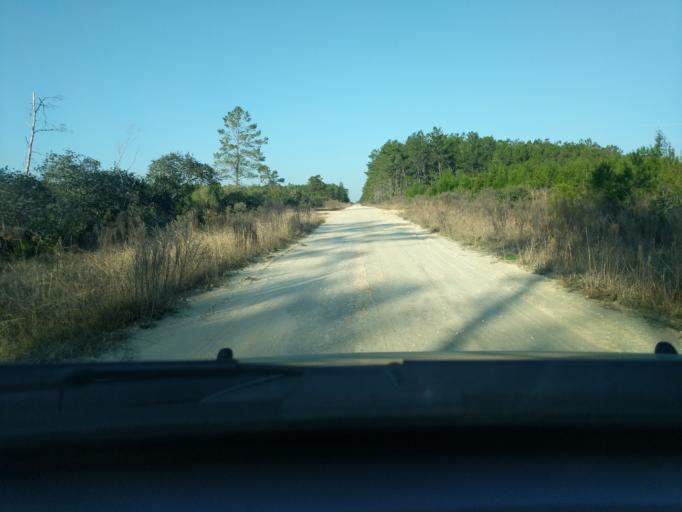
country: US
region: Florida
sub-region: Lake County
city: Astor
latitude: 29.2260
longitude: -81.7579
